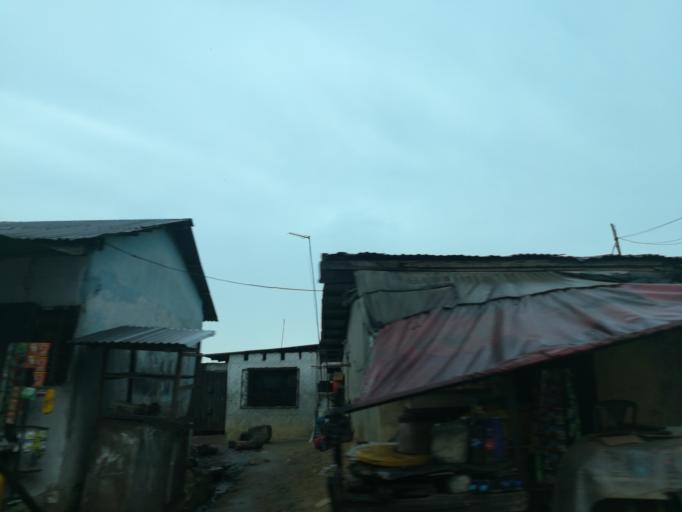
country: NG
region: Rivers
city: Port Harcourt
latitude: 4.7967
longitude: 6.9920
